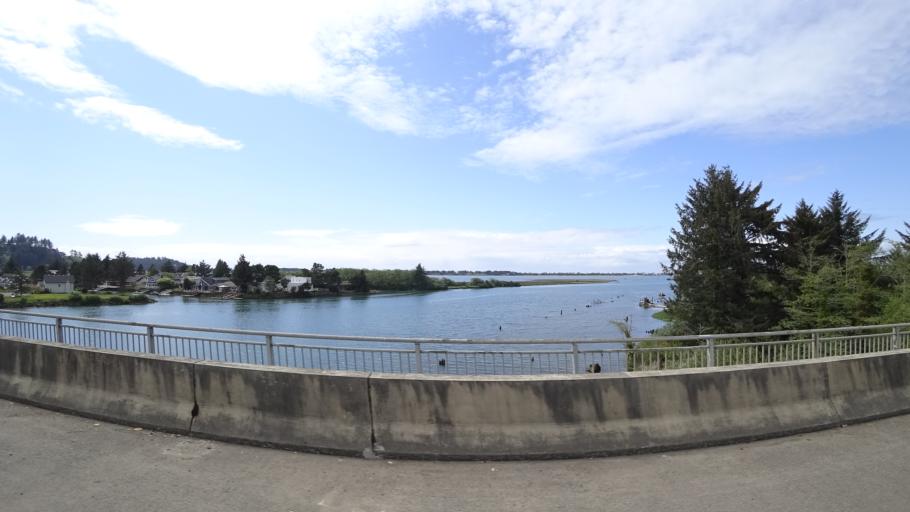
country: US
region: Oregon
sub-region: Lincoln County
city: Lincoln City
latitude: 44.9008
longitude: -124.0076
